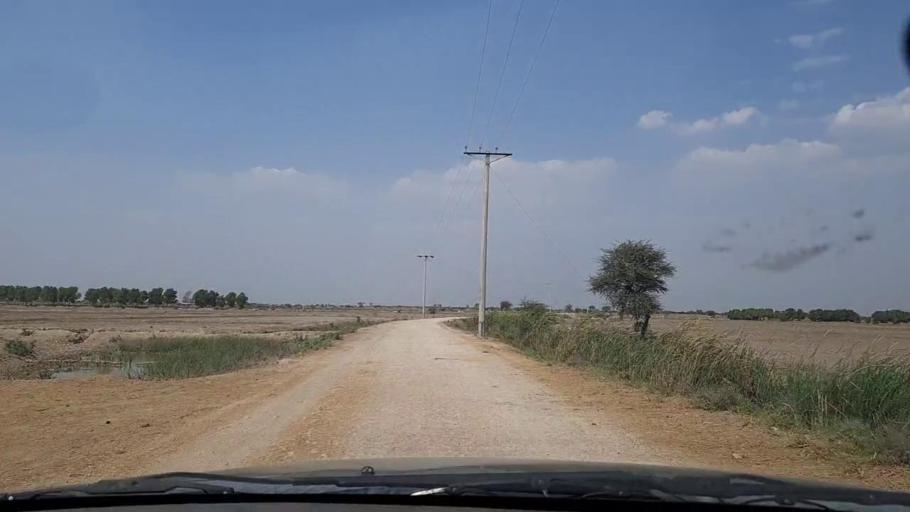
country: PK
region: Sindh
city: Mirpur Batoro
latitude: 24.6196
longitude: 68.2379
